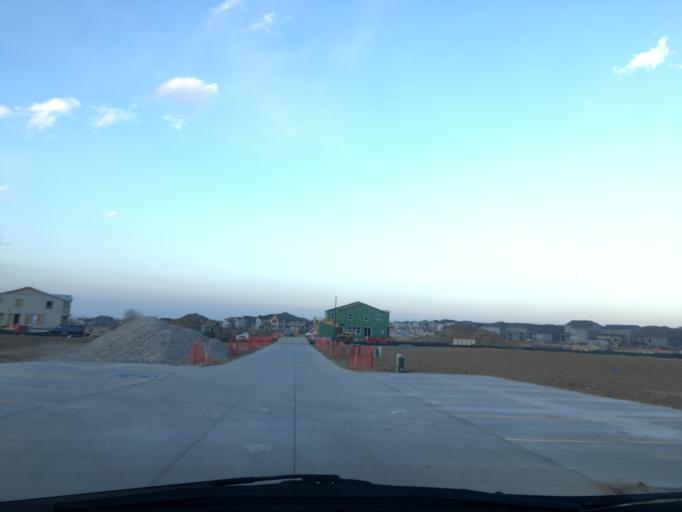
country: US
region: Colorado
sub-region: Boulder County
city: Lafayette
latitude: 40.0247
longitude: -105.0907
